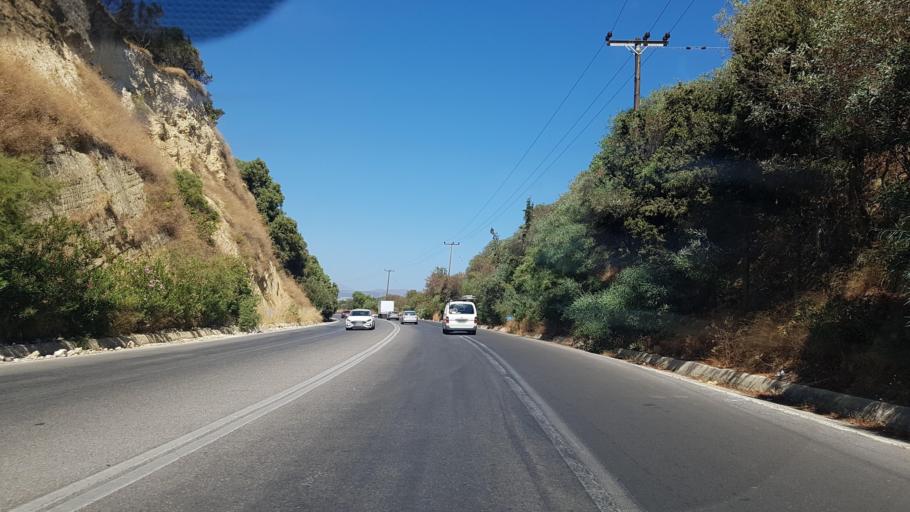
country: GR
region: Crete
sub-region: Nomos Chanias
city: Agia Marina
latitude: 35.5140
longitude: 23.9254
